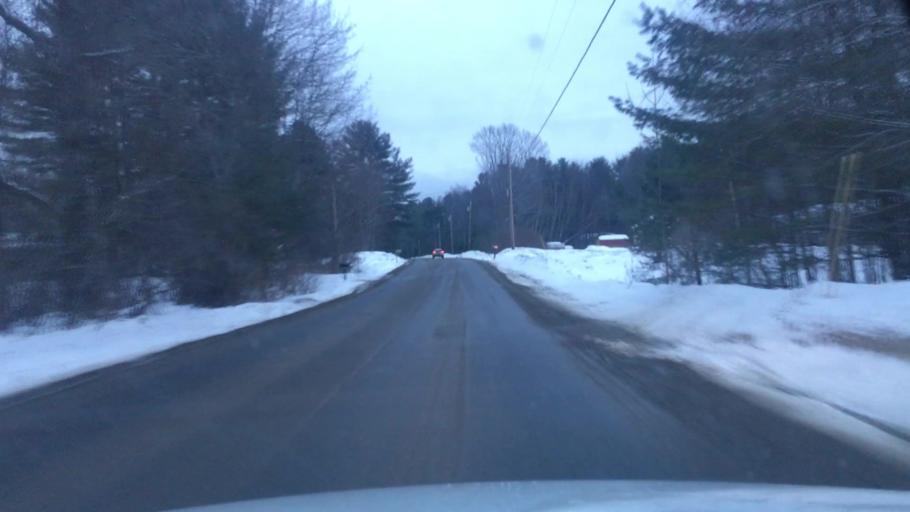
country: US
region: Maine
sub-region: Kennebec County
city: Oakland
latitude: 44.6254
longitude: -69.7289
